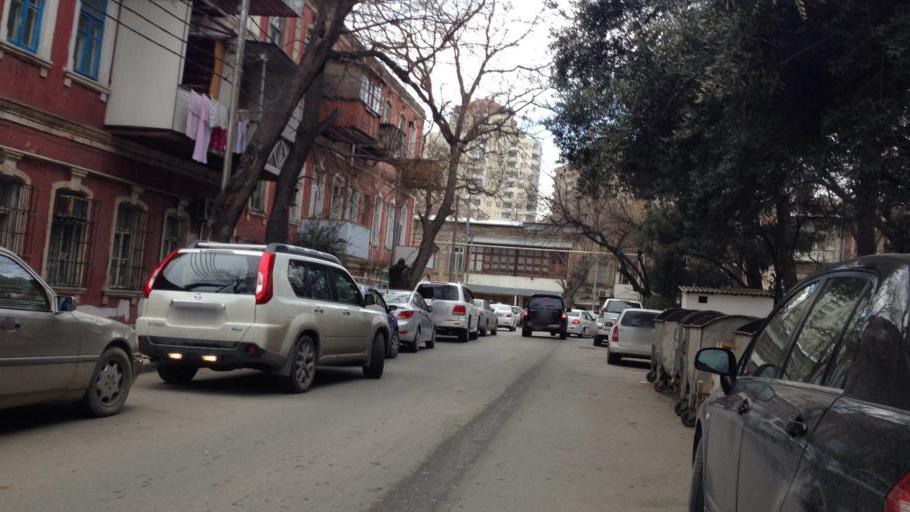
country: AZ
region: Baki
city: Baku
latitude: 40.3875
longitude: 49.8534
